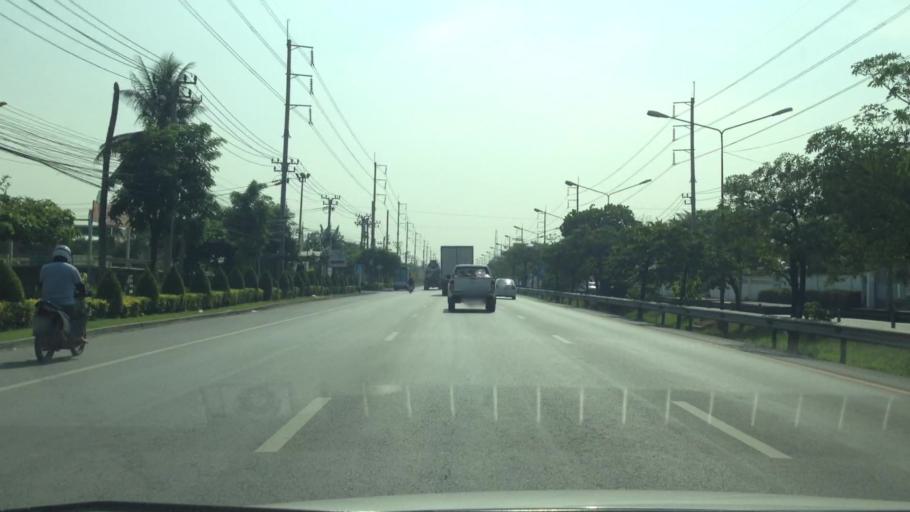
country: TH
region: Samut Prakan
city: Samut Prakan
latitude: 13.5309
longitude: 100.6326
